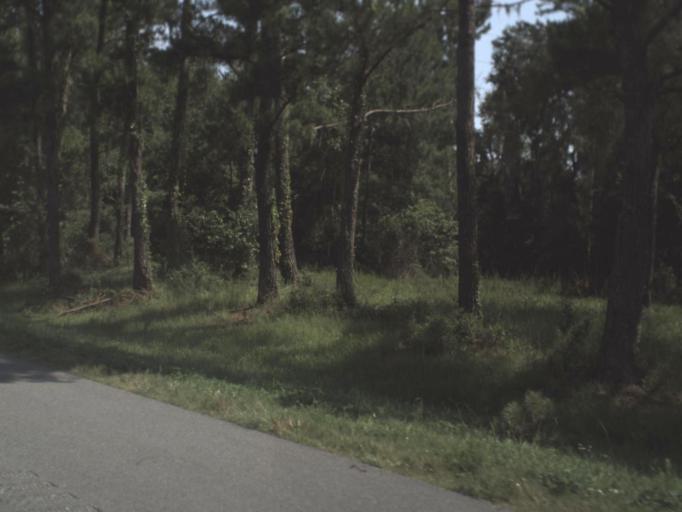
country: US
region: Florida
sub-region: Suwannee County
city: Wellborn
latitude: 30.3556
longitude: -82.8399
